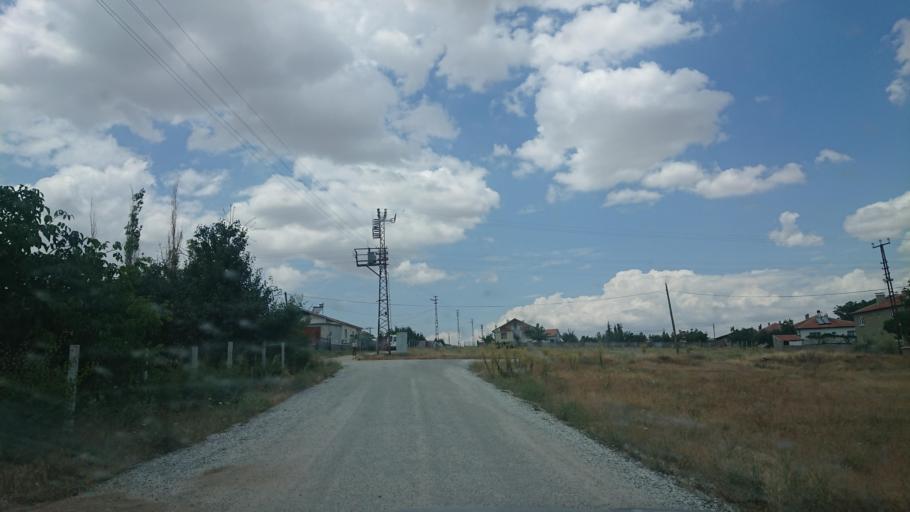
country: TR
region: Aksaray
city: Agacoren
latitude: 38.8735
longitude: 33.9079
